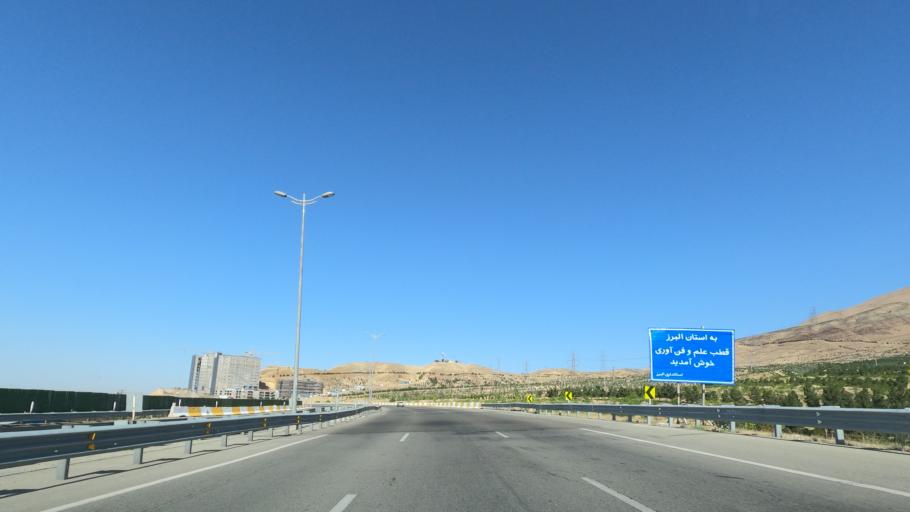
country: IR
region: Tehran
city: Shahr-e Qods
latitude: 35.7528
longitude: 51.1199
